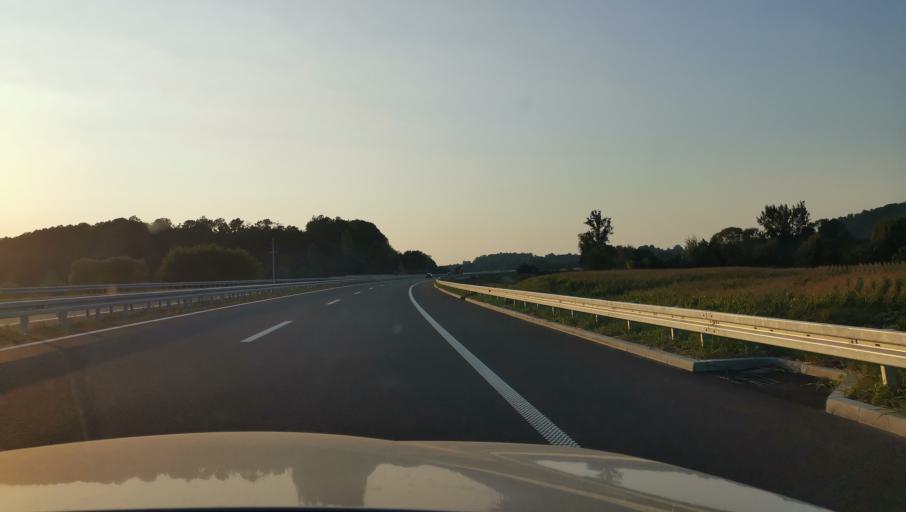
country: RS
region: Central Serbia
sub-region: Kolubarski Okrug
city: Lajkovac
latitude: 44.3363
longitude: 20.2010
